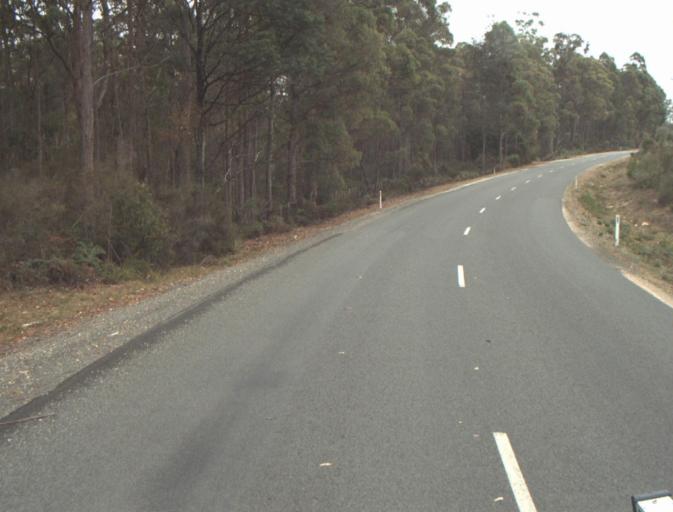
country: AU
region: Tasmania
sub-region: Dorset
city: Bridport
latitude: -41.1709
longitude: 147.2639
